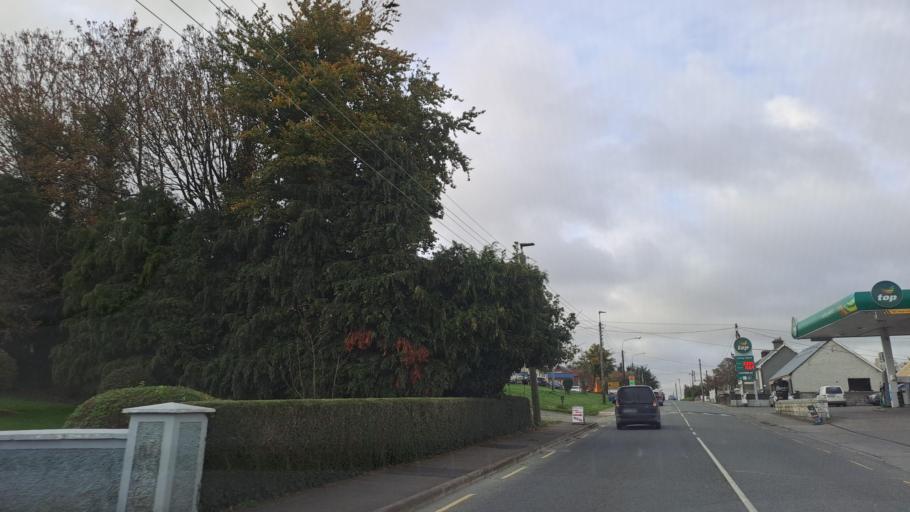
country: IE
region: Ulster
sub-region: An Cabhan
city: Kingscourt
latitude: 53.8995
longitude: -6.8033
